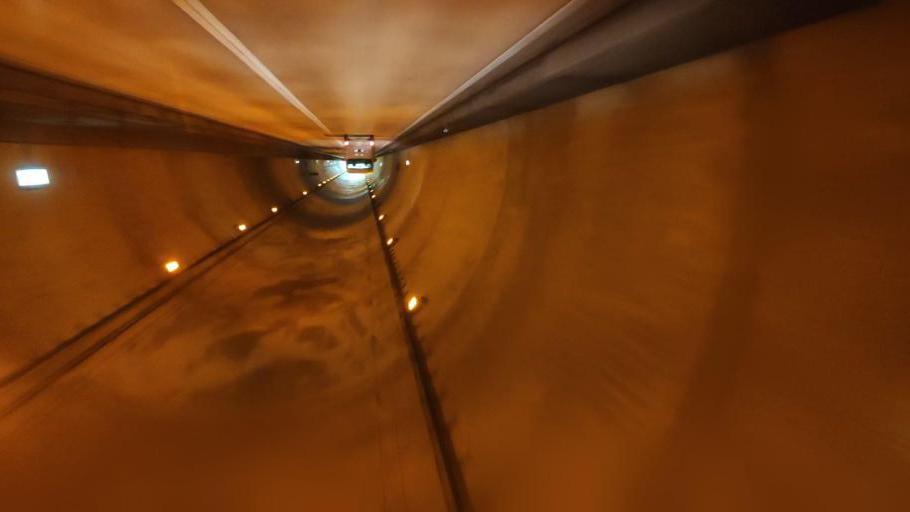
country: JP
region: Hyogo
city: Toyooka
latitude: 35.4924
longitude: 134.6215
